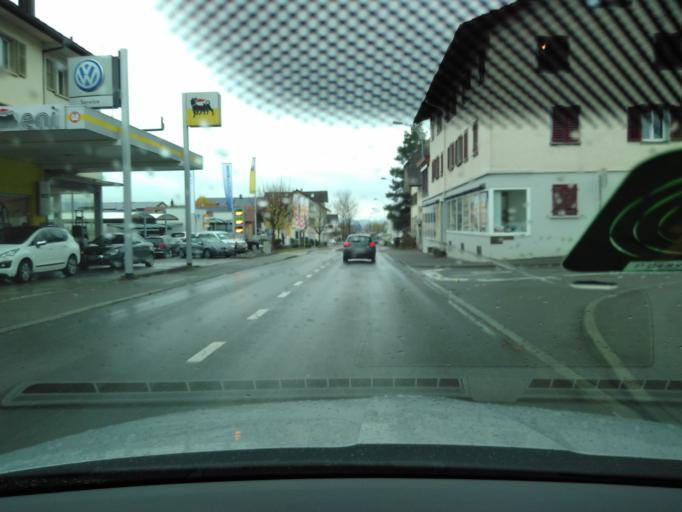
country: CH
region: Lucerne
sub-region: Sursee District
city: Triengen
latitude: 47.2371
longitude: 8.0754
